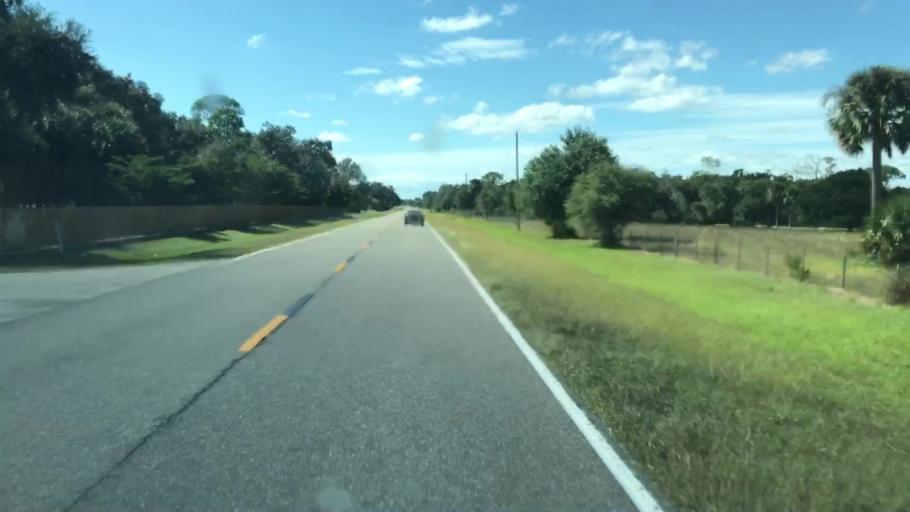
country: US
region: Florida
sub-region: Lee County
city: Olga
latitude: 26.7400
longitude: -81.7309
